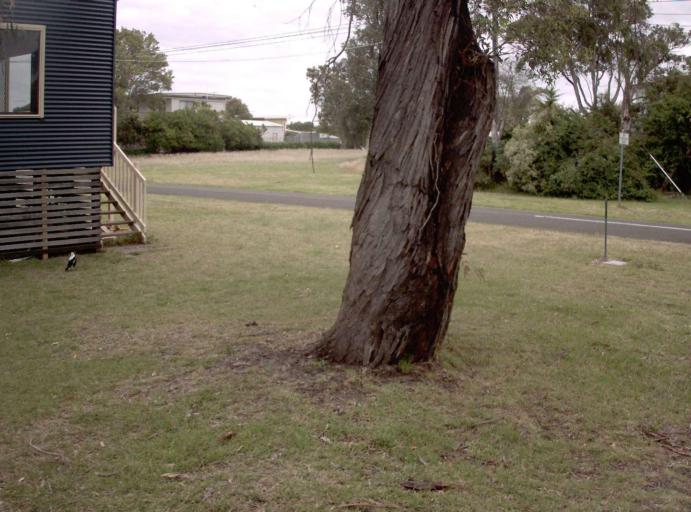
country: AU
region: Victoria
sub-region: East Gippsland
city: Bairnsdale
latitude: -38.0539
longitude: 147.5733
